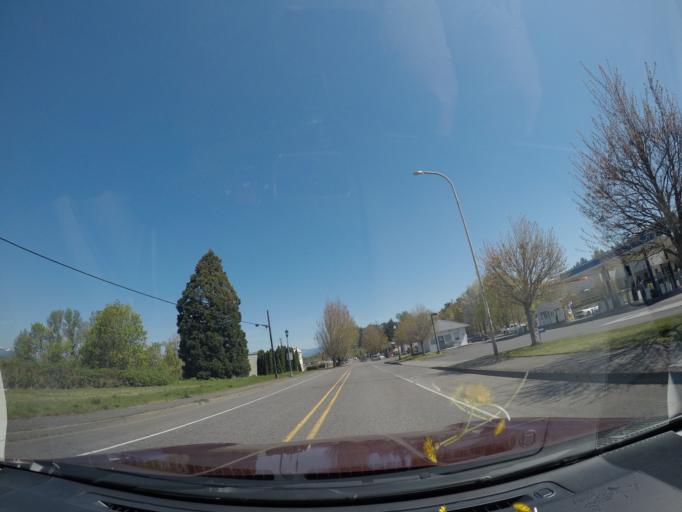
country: US
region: Oregon
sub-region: Multnomah County
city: Troutdale
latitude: 45.5407
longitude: -122.3933
